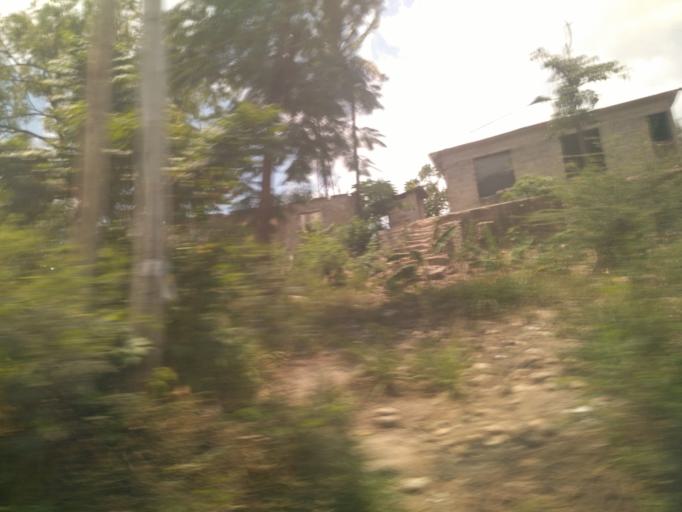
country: TZ
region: Dar es Salaam
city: Dar es Salaam
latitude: -6.8857
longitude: 39.2719
